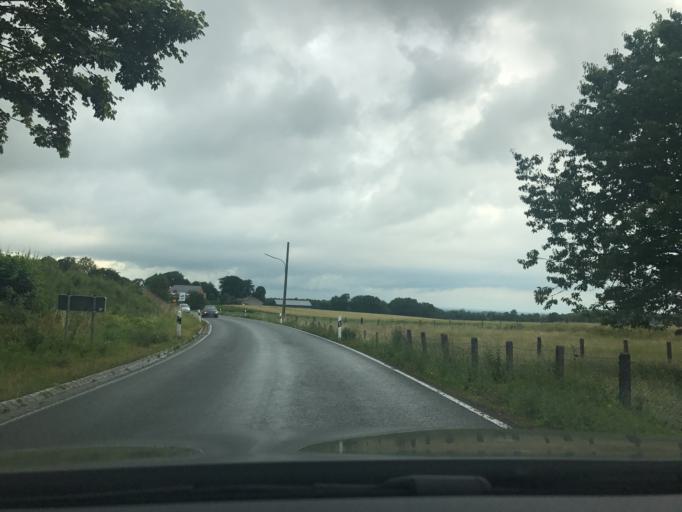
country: DE
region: North Rhine-Westphalia
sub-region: Regierungsbezirk Arnsberg
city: Mohnesee
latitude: 51.5248
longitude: 8.1678
